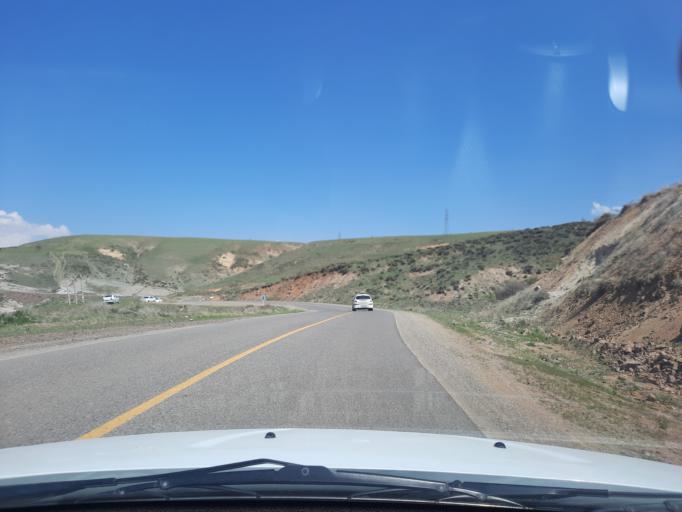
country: IR
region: Qazvin
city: Qazvin
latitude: 36.4076
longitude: 50.2317
